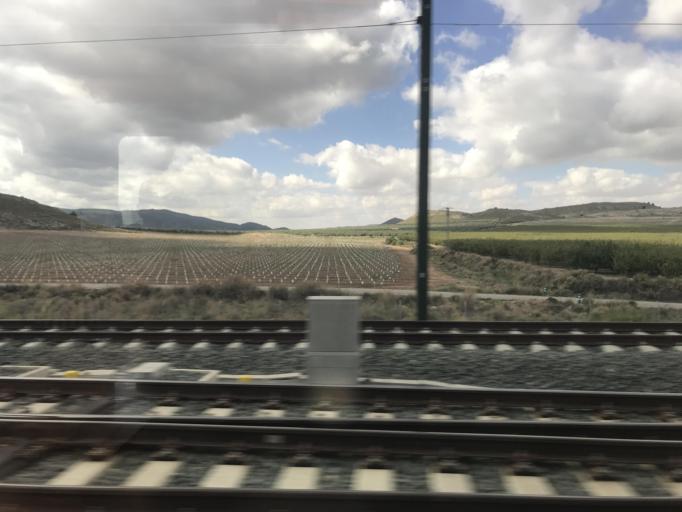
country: ES
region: Valencia
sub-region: Provincia de Alicante
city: Villena
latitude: 38.5892
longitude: -0.8754
